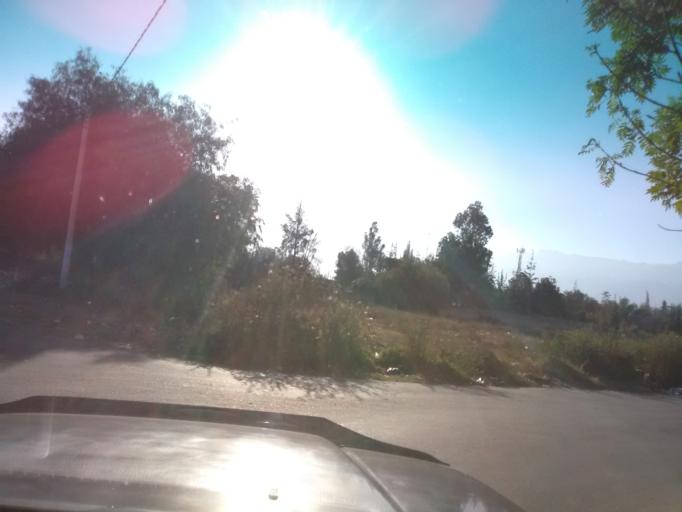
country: BO
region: Cochabamba
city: Cochabamba
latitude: -17.3810
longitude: -66.2007
